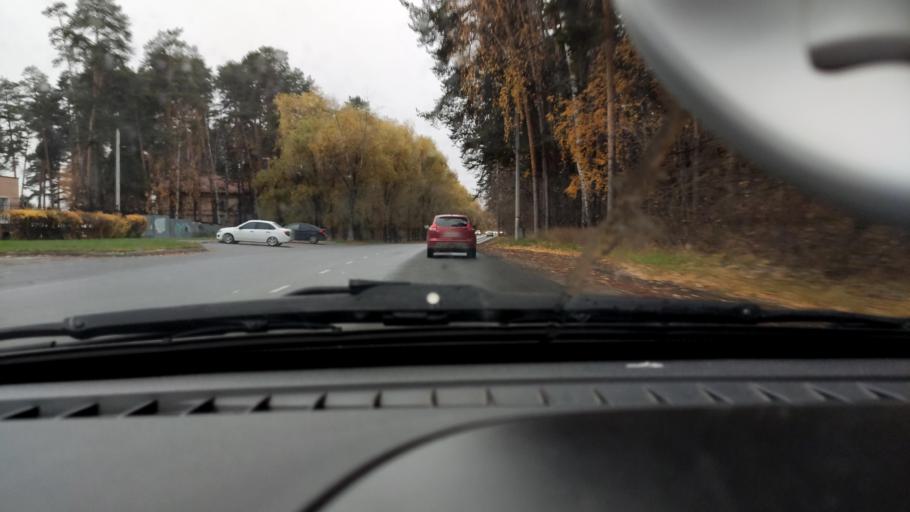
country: RU
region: Perm
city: Kultayevo
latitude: 58.0100
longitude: 55.9789
